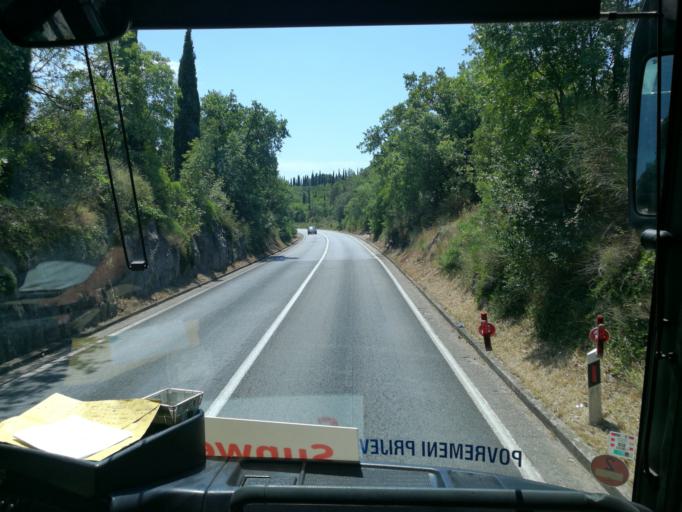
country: HR
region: Dubrovacko-Neretvanska
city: Cavtat
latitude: 42.5682
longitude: 18.2451
